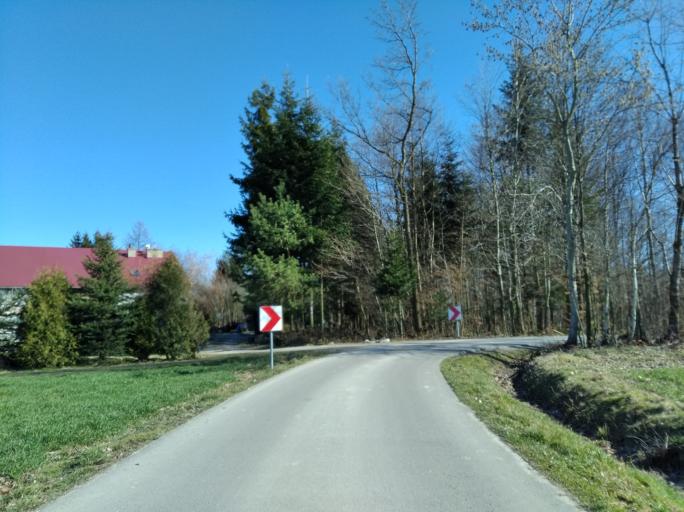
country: PL
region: Subcarpathian Voivodeship
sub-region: Powiat strzyzowski
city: Wisniowa
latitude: 49.9024
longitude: 21.7076
